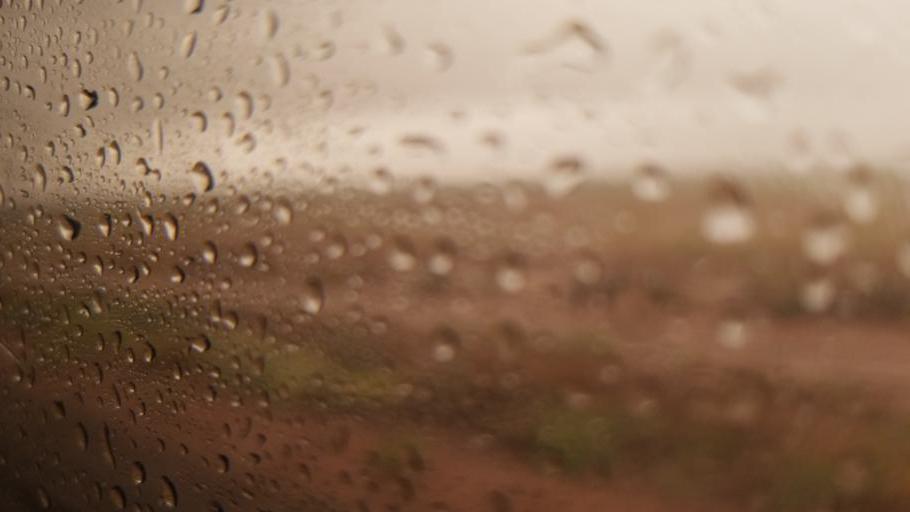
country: US
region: Arizona
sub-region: Navajo County
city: Joseph City
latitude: 34.9444
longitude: -110.3238
